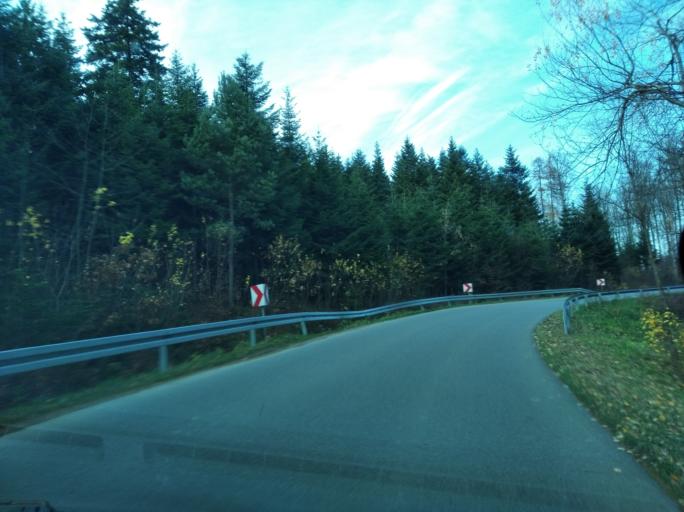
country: PL
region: Subcarpathian Voivodeship
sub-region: Powiat ropczycko-sedziszowski
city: Zagorzyce
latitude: 49.9623
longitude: 21.6907
